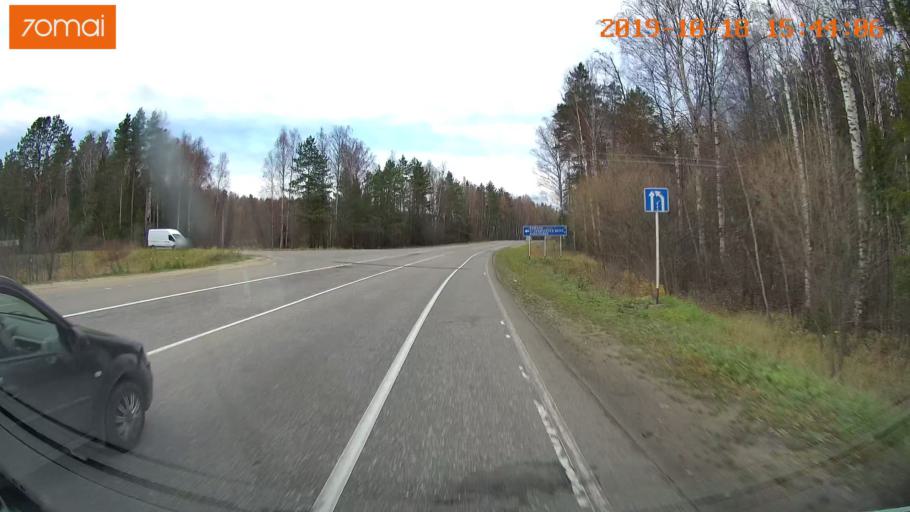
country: RU
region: Vladimir
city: Golovino
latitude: 55.9770
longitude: 40.5471
